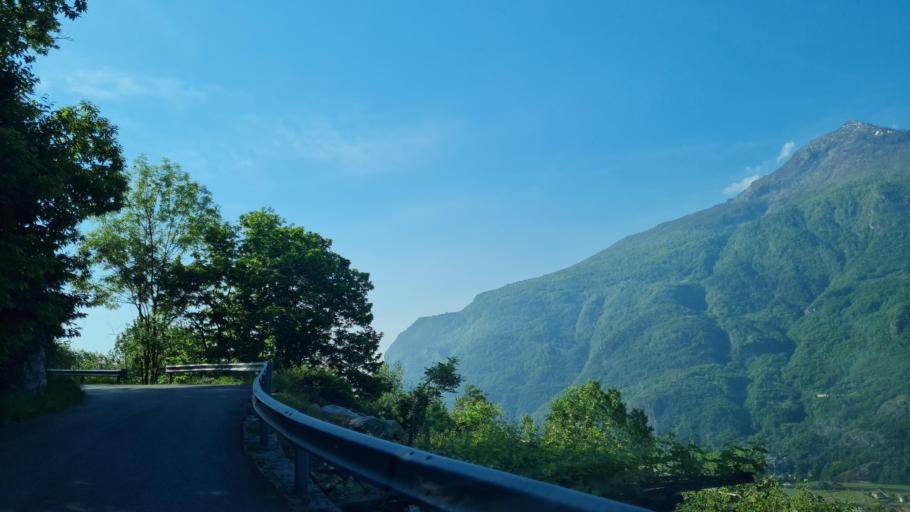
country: IT
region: Aosta Valley
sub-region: Valle d'Aosta
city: Donnas
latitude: 45.6102
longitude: 7.7676
